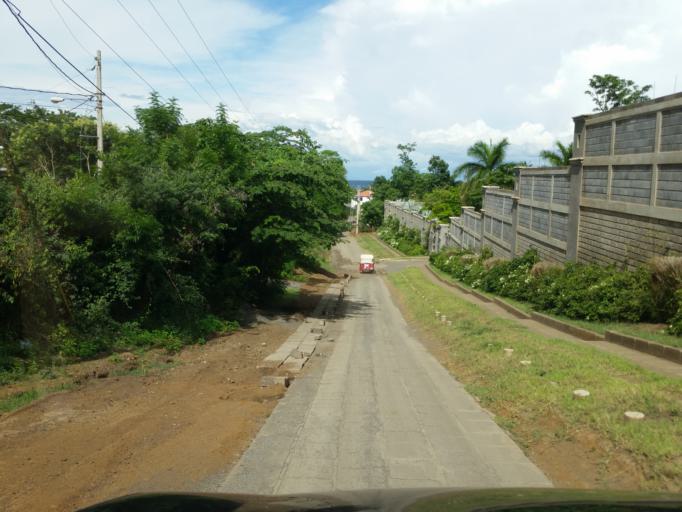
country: NI
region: Managua
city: Managua
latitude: 12.0738
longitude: -86.2416
